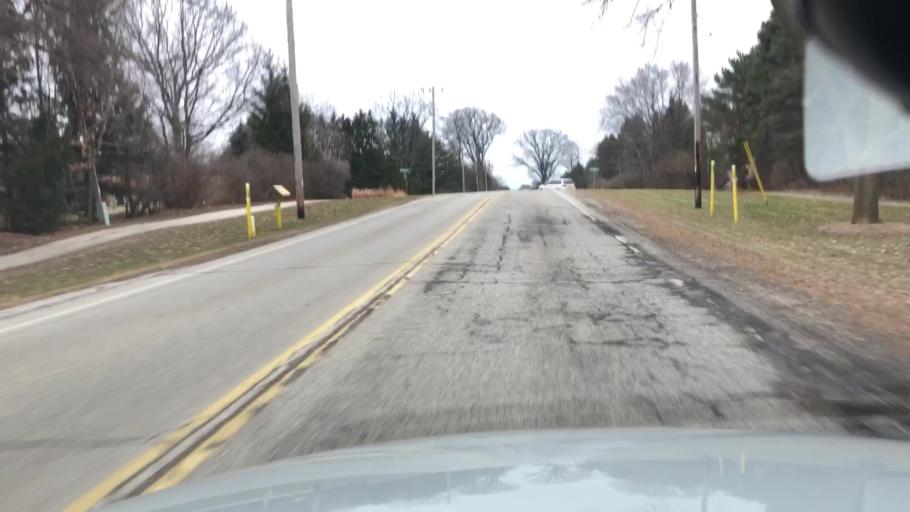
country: US
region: Wisconsin
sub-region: Waukesha County
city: Brookfield
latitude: 43.0611
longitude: -88.1362
